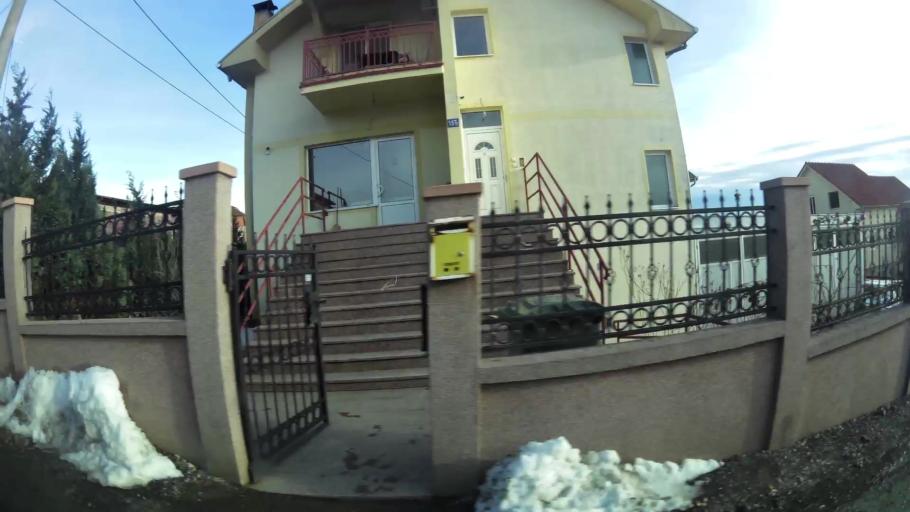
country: RS
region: Central Serbia
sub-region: Belgrade
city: Rakovica
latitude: 44.7380
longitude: 20.4540
